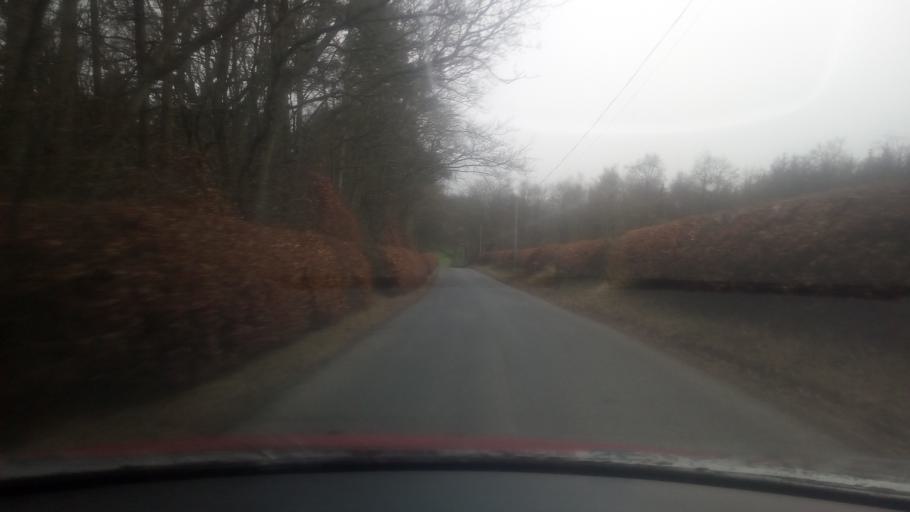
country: GB
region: Scotland
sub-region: The Scottish Borders
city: Hawick
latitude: 55.3837
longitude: -2.6569
